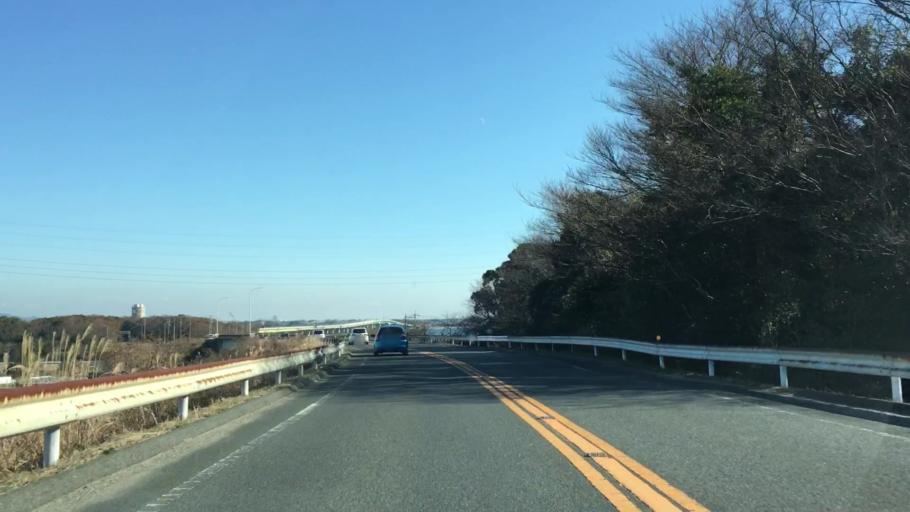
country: JP
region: Aichi
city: Tahara
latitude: 34.6934
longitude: 137.2861
